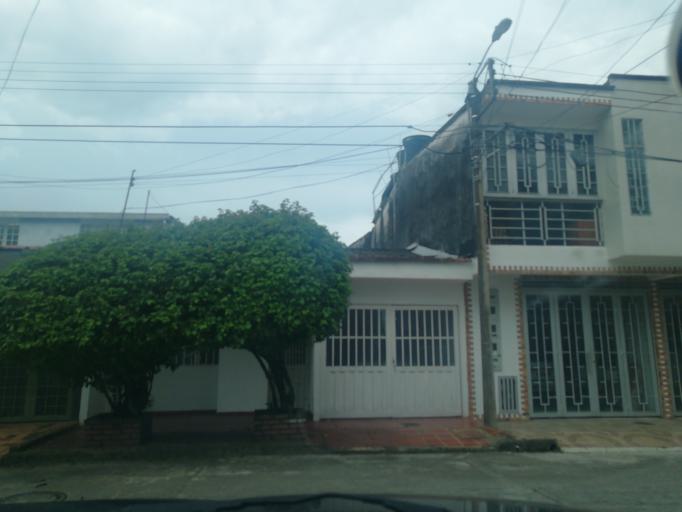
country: CO
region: Meta
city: Acacias
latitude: 3.9854
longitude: -73.7700
